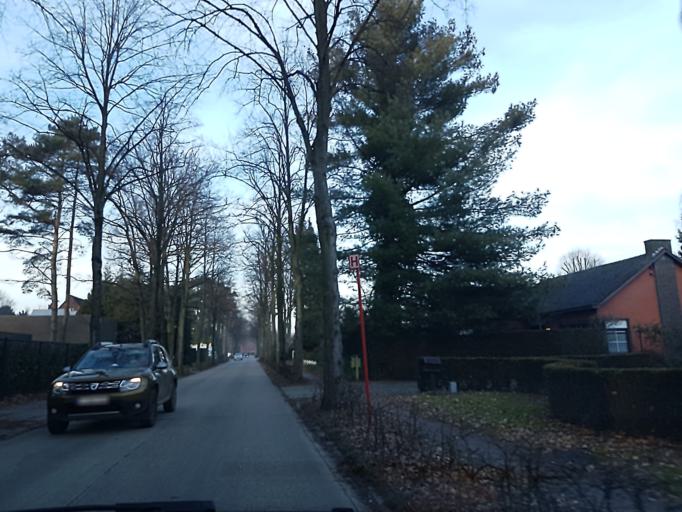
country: BE
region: Flanders
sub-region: Provincie Antwerpen
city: Zandhoven
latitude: 51.2447
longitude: 4.6469
